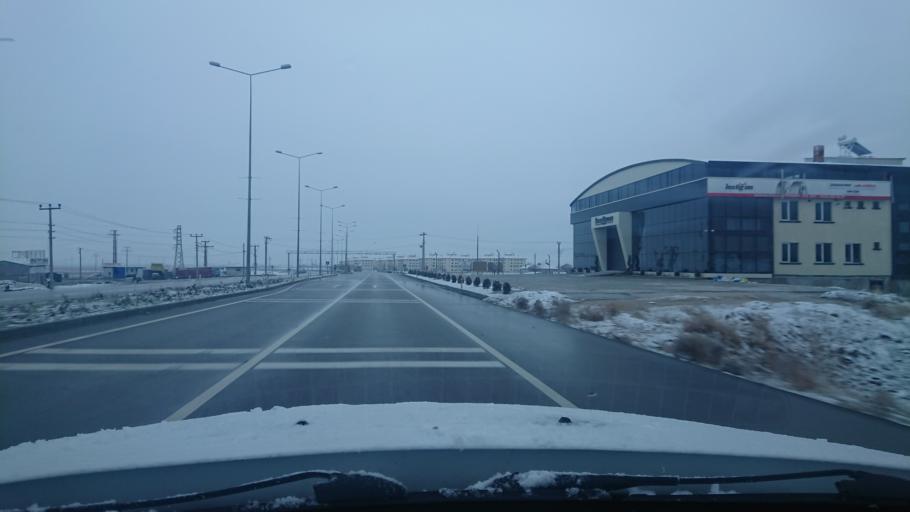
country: TR
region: Aksaray
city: Sultanhani
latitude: 38.2528
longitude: 33.5641
